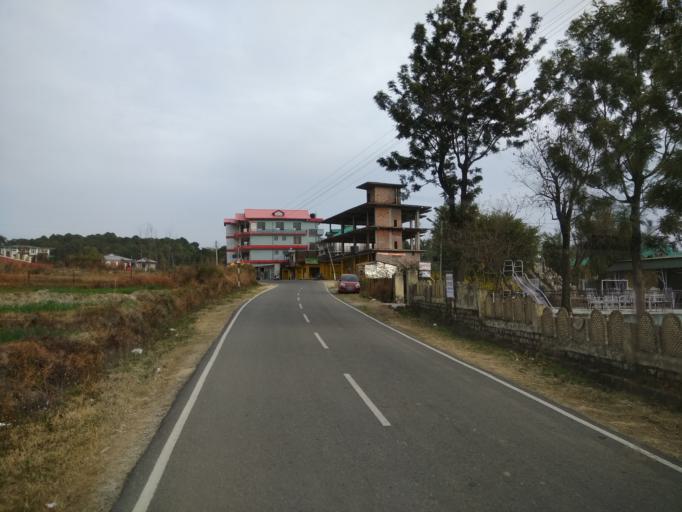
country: IN
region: Himachal Pradesh
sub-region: Kangra
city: Palampur
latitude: 32.1115
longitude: 76.5013
